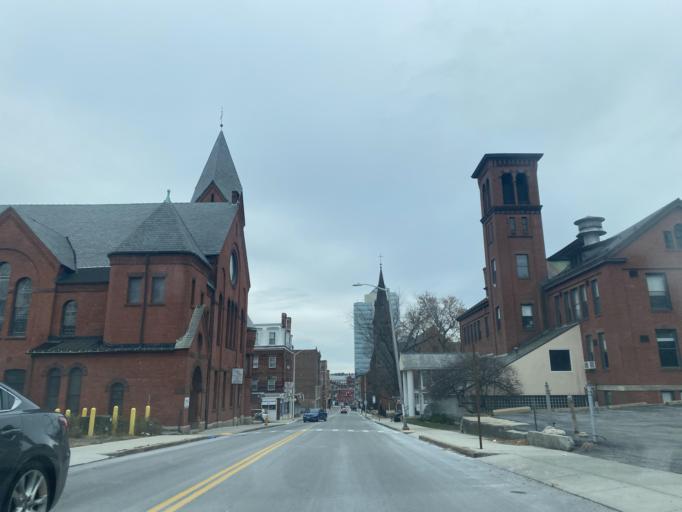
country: US
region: Massachusetts
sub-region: Worcester County
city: Worcester
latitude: 42.2639
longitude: -71.8083
